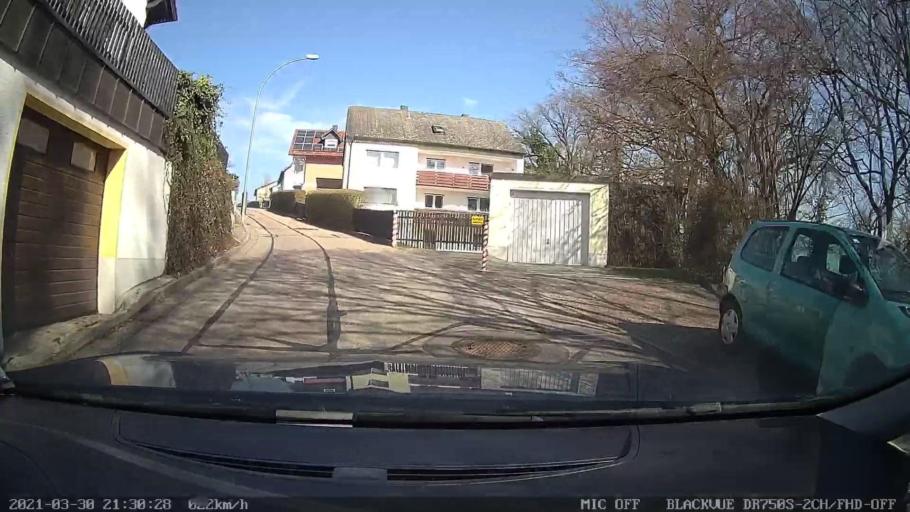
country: DE
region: Bavaria
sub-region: Upper Palatinate
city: Zeitlarn
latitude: 49.0959
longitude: 12.1057
